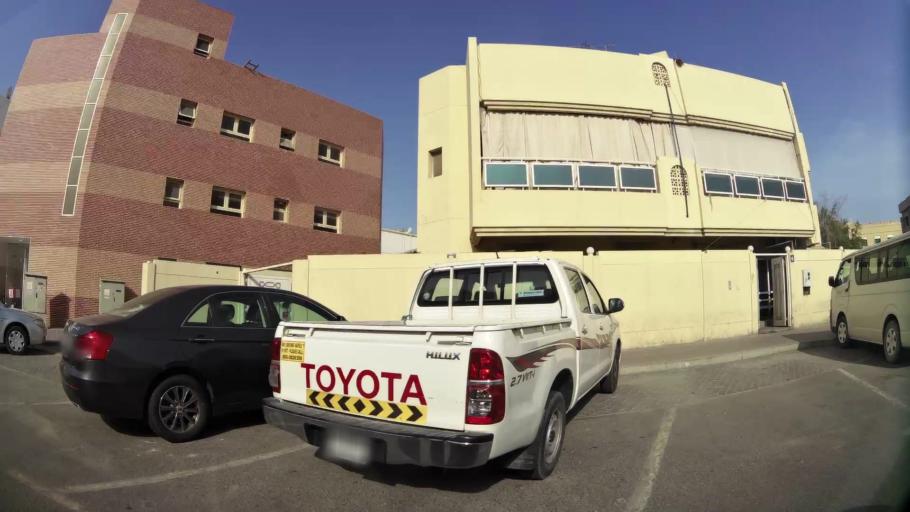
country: AE
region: Ash Shariqah
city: Sharjah
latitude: 25.2788
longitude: 55.3347
